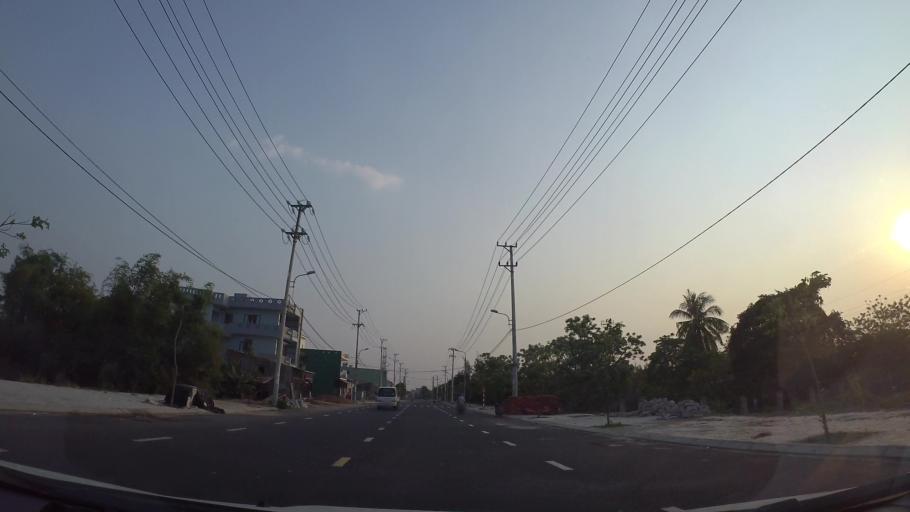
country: VN
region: Da Nang
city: Ngu Hanh Son
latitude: 15.9739
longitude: 108.2325
